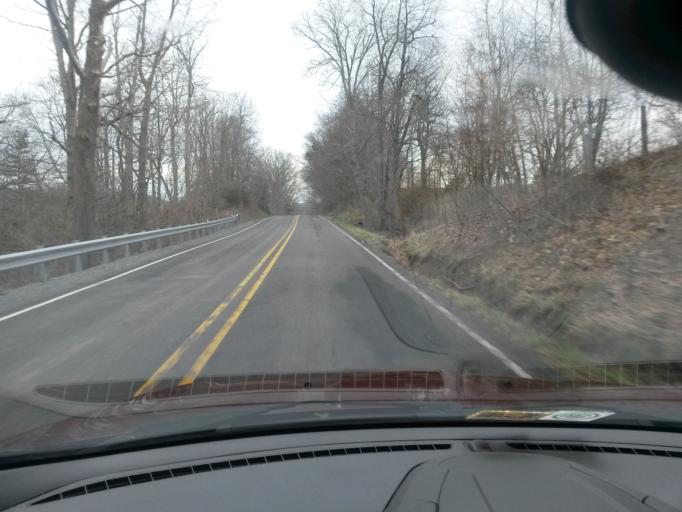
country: US
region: Virginia
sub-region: Bath County
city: Warm Springs
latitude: 38.1944
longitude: -79.7321
